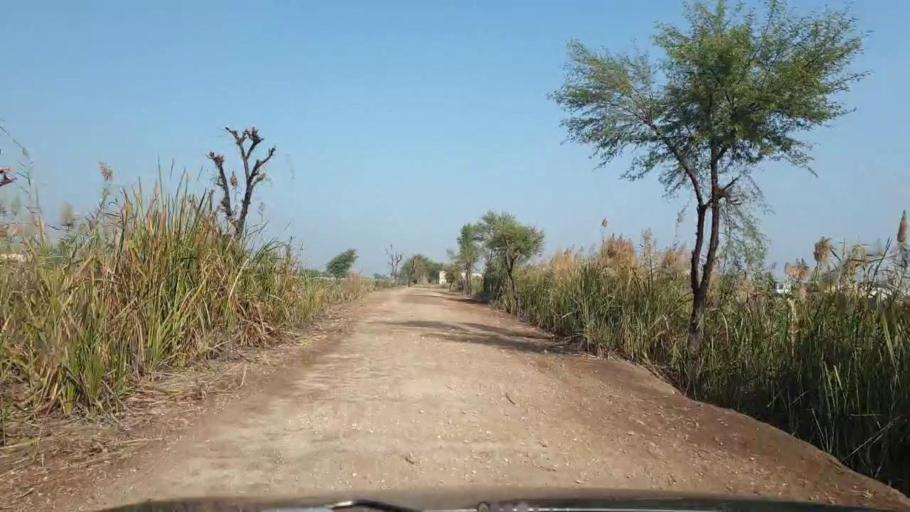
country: PK
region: Sindh
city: Sinjhoro
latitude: 26.0665
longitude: 68.7724
